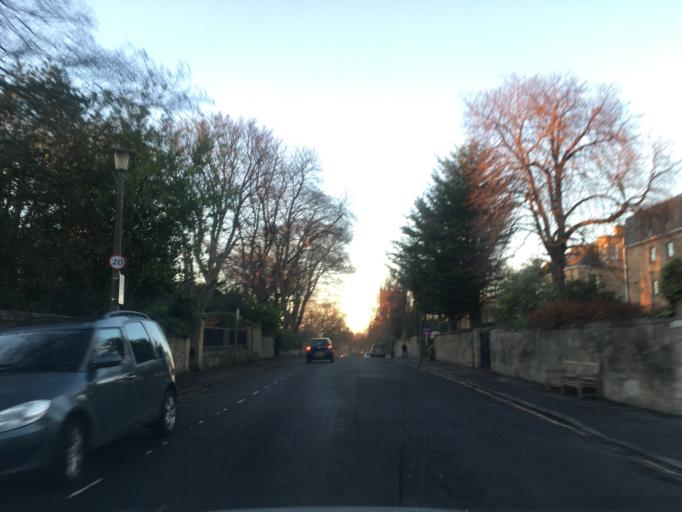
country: GB
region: Scotland
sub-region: Edinburgh
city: Edinburgh
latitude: 55.9321
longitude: -3.2216
